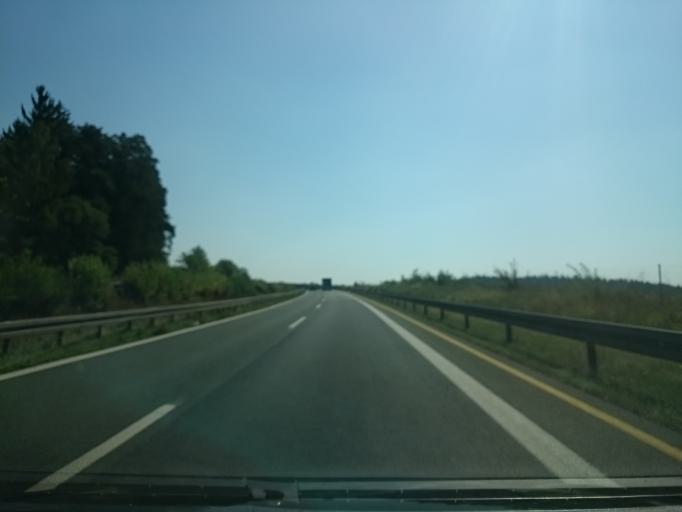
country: DE
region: Bavaria
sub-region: Upper Franconia
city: Wonsees
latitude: 50.0064
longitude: 11.2537
